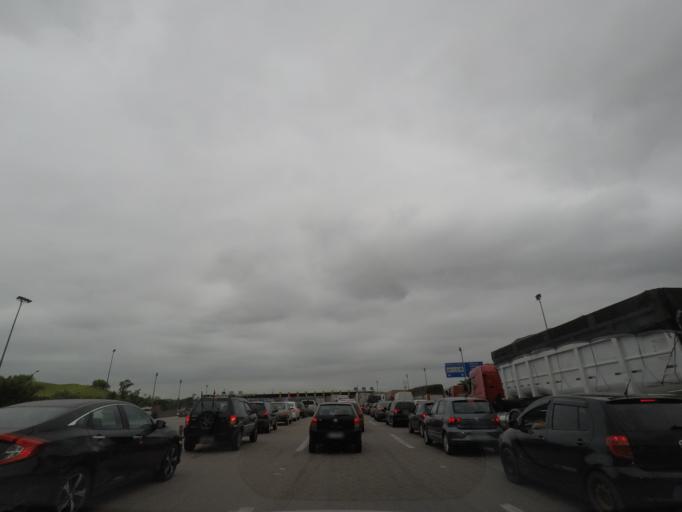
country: BR
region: Sao Paulo
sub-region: Jacarei
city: Jacarei
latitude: -23.2976
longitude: -46.0092
